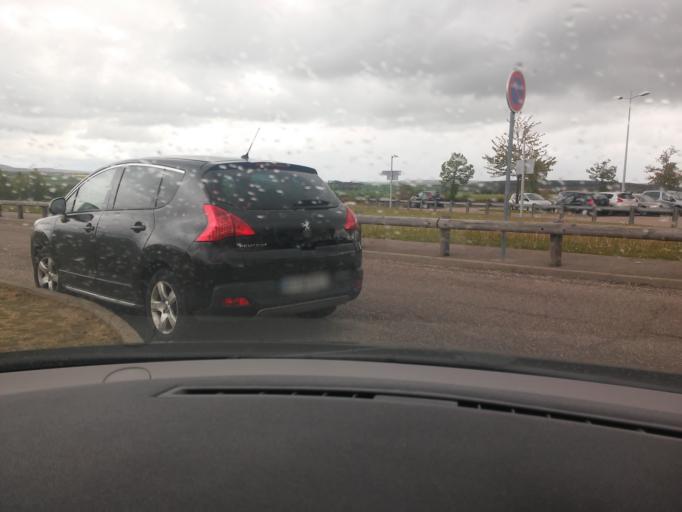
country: FR
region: Lorraine
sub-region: Departement de la Moselle
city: Verny
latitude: 48.9483
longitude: 6.1699
